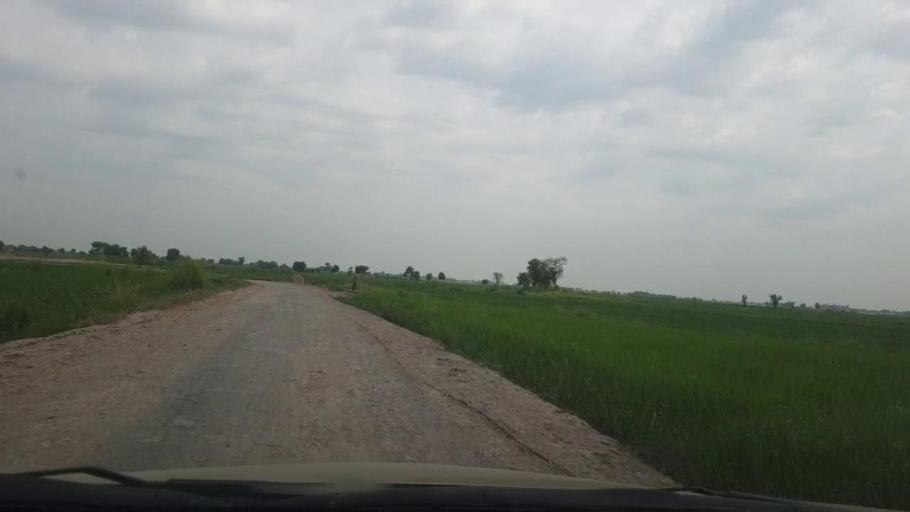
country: PK
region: Sindh
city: Ratodero
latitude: 27.7136
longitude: 68.2290
